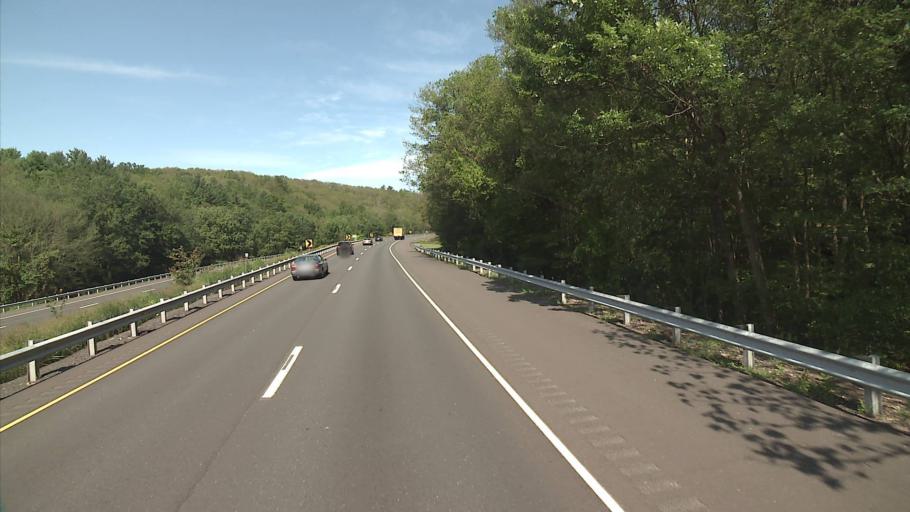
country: US
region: Connecticut
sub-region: Hartford County
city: Terramuggus
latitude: 41.6516
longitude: -72.4967
